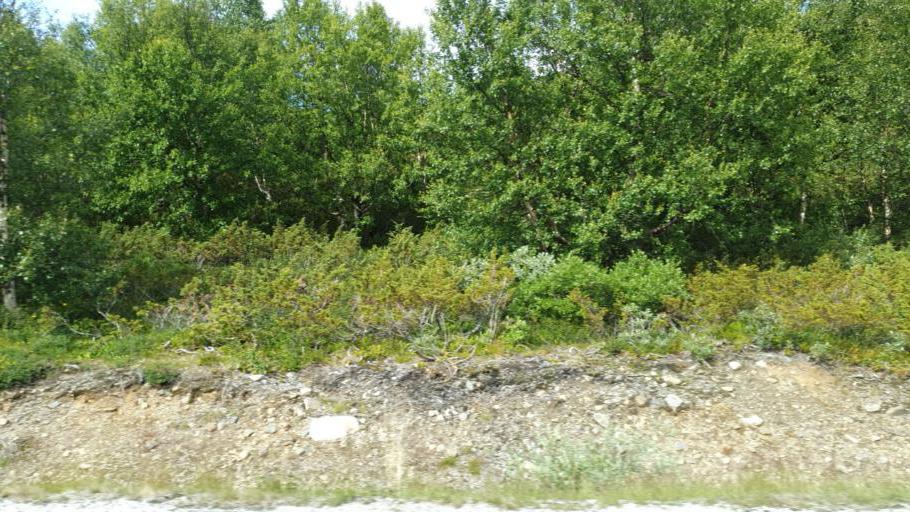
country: NO
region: Oppland
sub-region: Vaga
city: Vagamo
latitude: 61.5184
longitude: 8.8634
